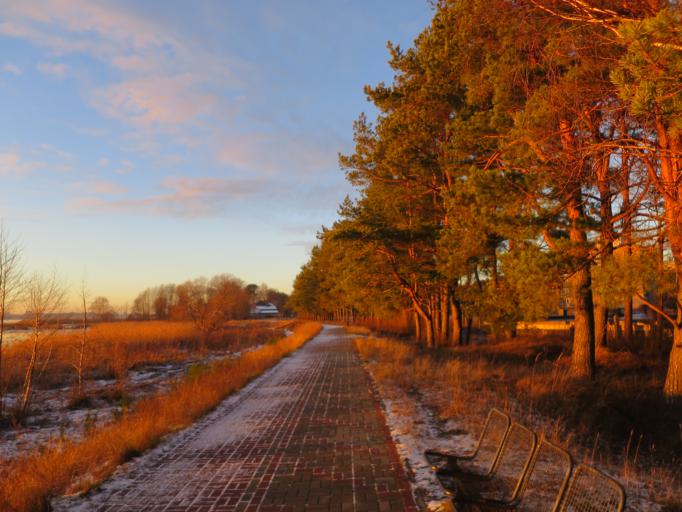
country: LV
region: Riga
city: Bergi
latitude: 56.9771
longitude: 24.3052
